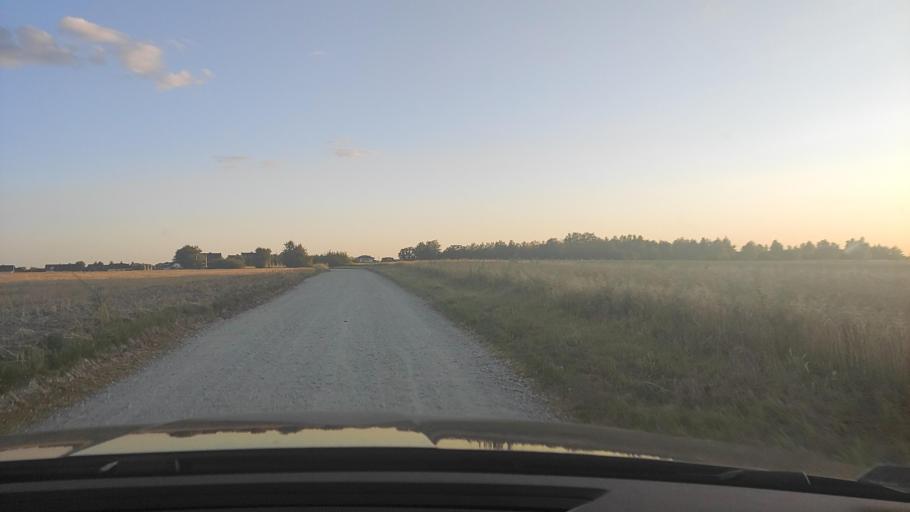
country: PL
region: Greater Poland Voivodeship
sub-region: Powiat poznanski
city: Swarzedz
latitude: 52.4358
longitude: 17.1188
